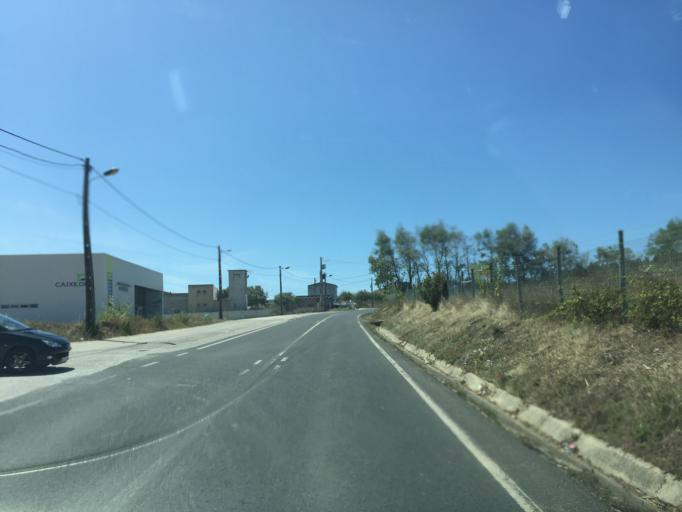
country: PT
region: Lisbon
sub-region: Lourinha
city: Lourinha
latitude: 39.2288
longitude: -9.3118
